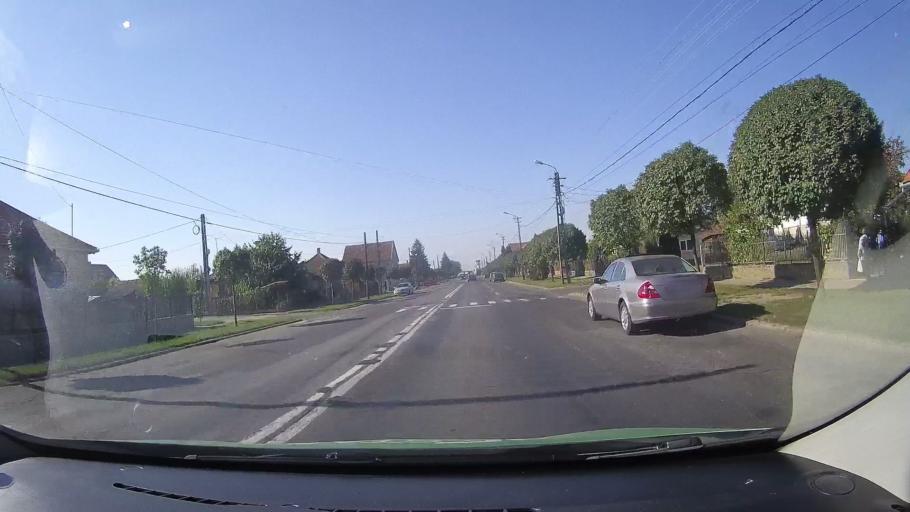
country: RO
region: Satu Mare
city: Carei
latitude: 47.6766
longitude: 22.4505
